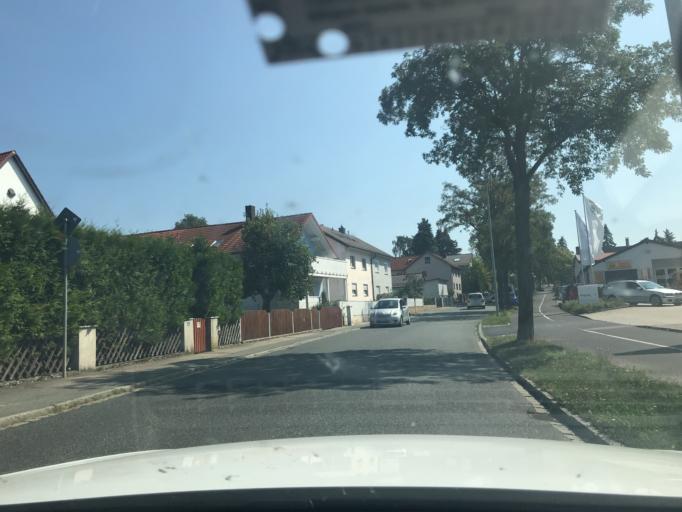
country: DE
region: Bavaria
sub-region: Upper Palatinate
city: Amberg
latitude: 49.4496
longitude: 11.8295
